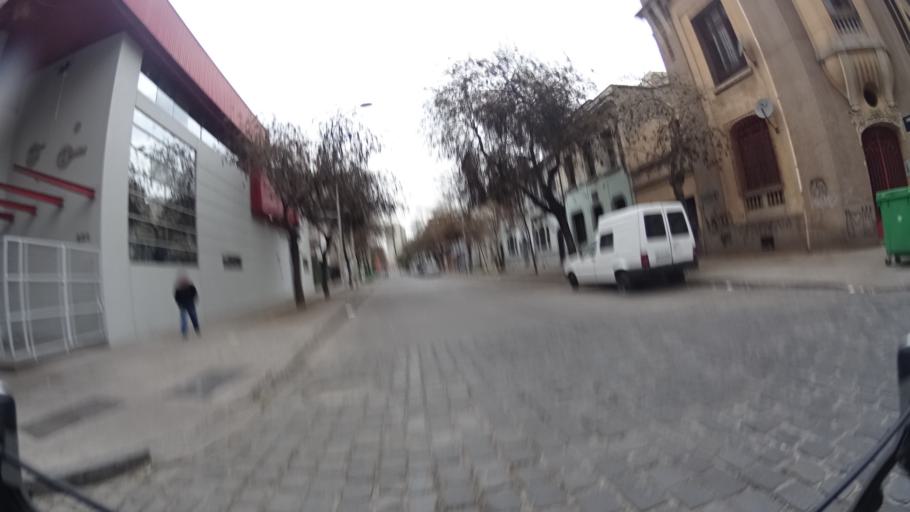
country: CL
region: Santiago Metropolitan
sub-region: Provincia de Santiago
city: Santiago
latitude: -33.4556
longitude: -70.6611
